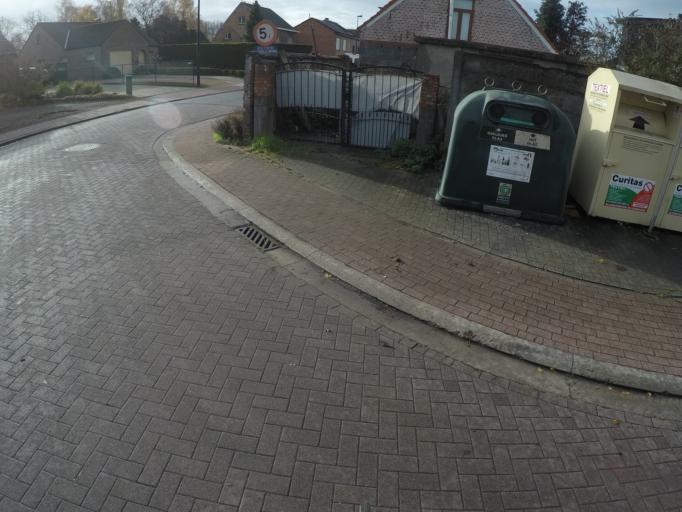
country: BE
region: Flanders
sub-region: Provincie Vlaams-Brabant
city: Londerzeel
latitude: 51.0291
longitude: 4.3071
